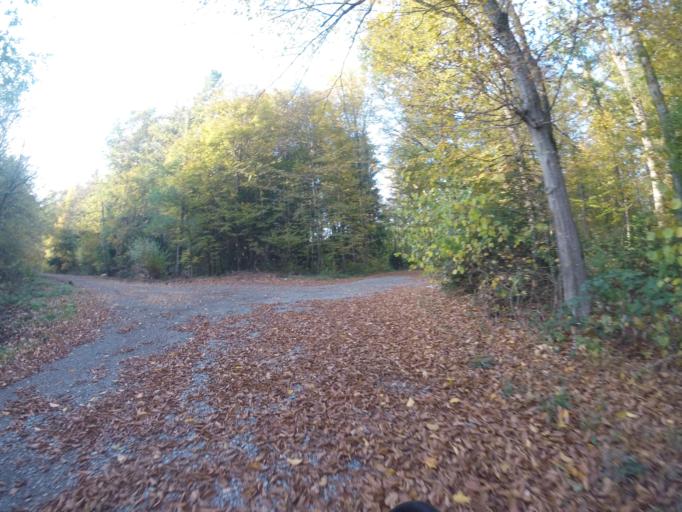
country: DE
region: Baden-Wuerttemberg
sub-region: Regierungsbezirk Stuttgart
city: Aspach
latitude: 48.9830
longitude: 9.3928
